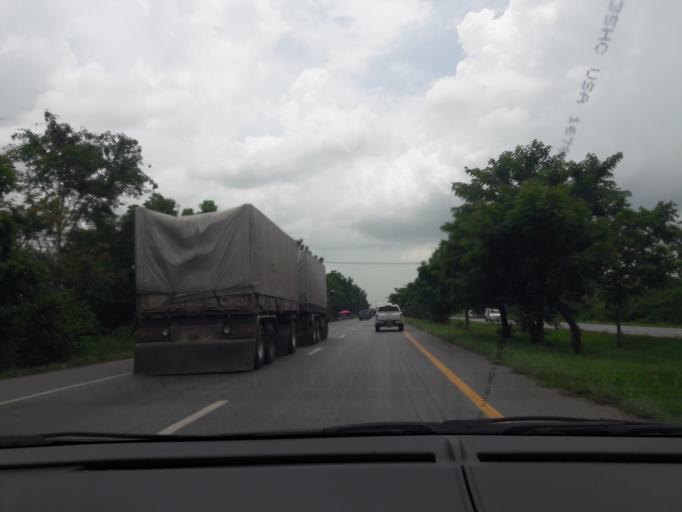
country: TH
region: Nakhon Ratchasima
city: Chaloem Phra Kiat
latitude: 15.0667
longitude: 102.1947
